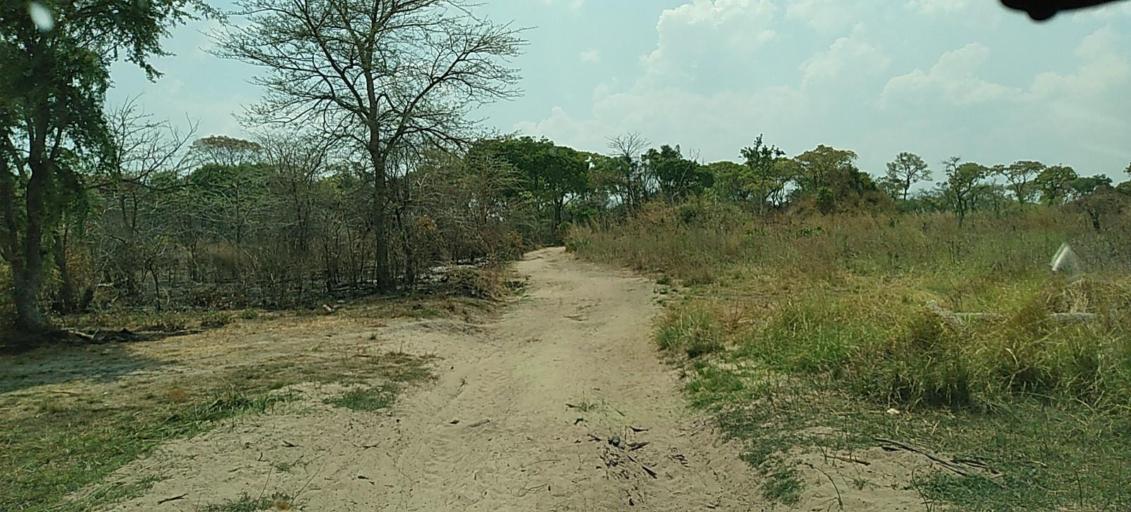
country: ZM
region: North-Western
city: Kabompo
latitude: -13.6343
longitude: 24.3851
